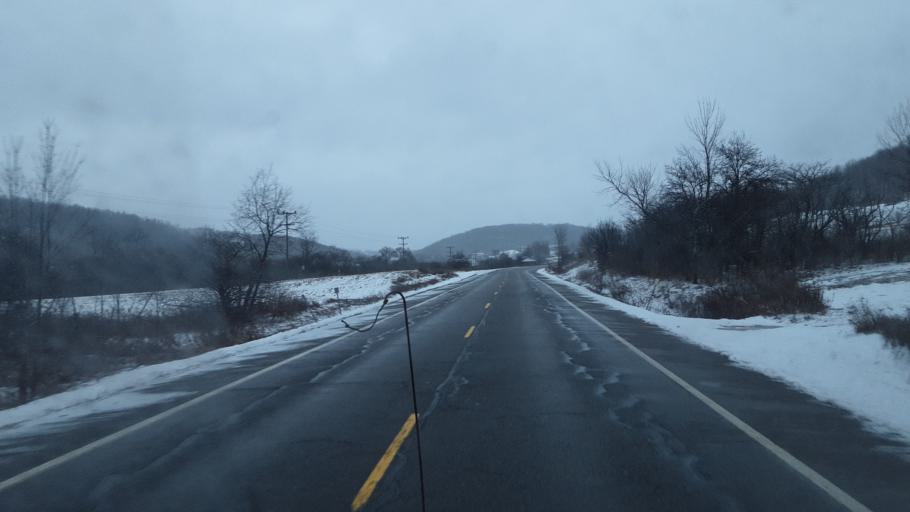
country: US
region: Pennsylvania
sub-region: Tioga County
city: Westfield
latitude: 42.0701
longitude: -77.5492
